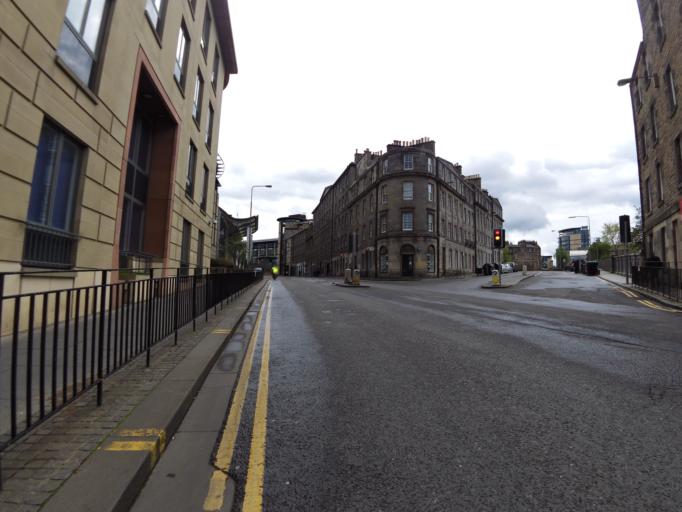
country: GB
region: Scotland
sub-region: Edinburgh
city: Edinburgh
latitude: 55.9460
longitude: -3.2109
